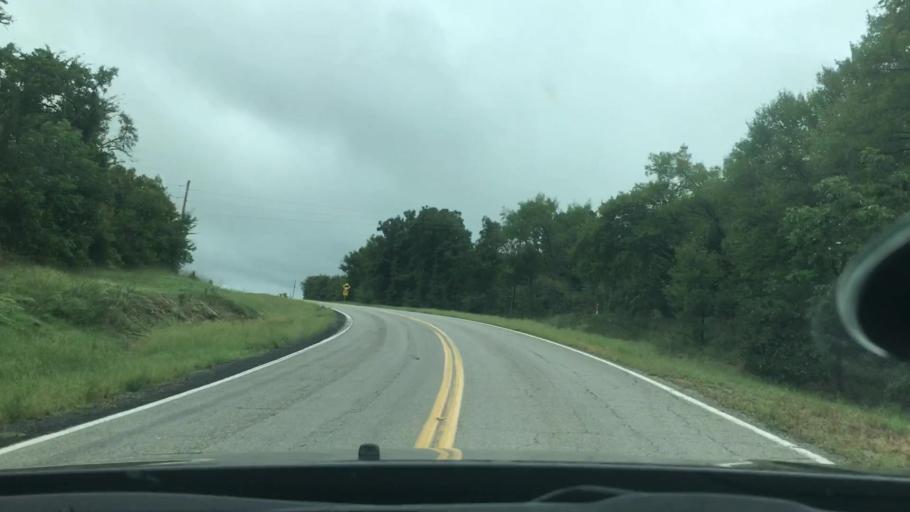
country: US
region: Oklahoma
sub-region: Cherokee County
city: Park Hill
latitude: 35.6886
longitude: -94.9107
